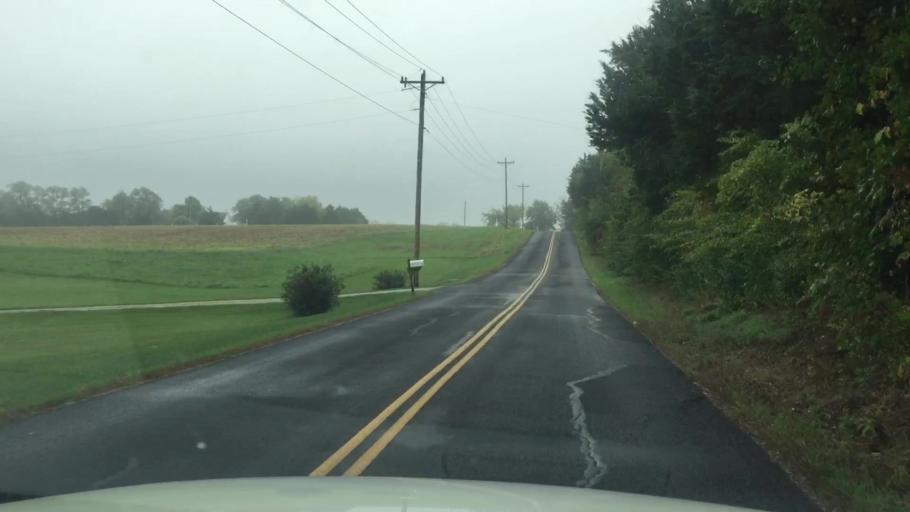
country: US
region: Missouri
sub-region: Boone County
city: Ashland
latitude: 38.8175
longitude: -92.2926
